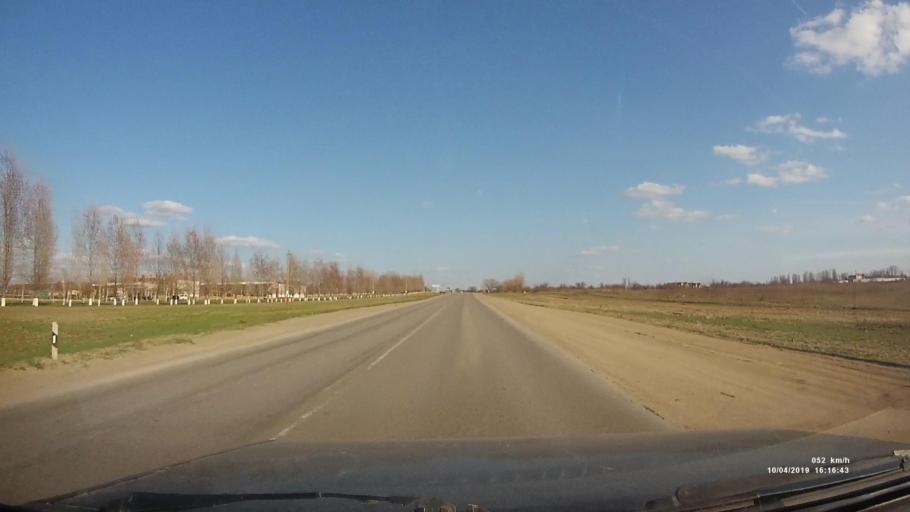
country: RU
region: Rostov
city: Staraya Stanitsa
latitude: 48.3273
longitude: 40.3123
